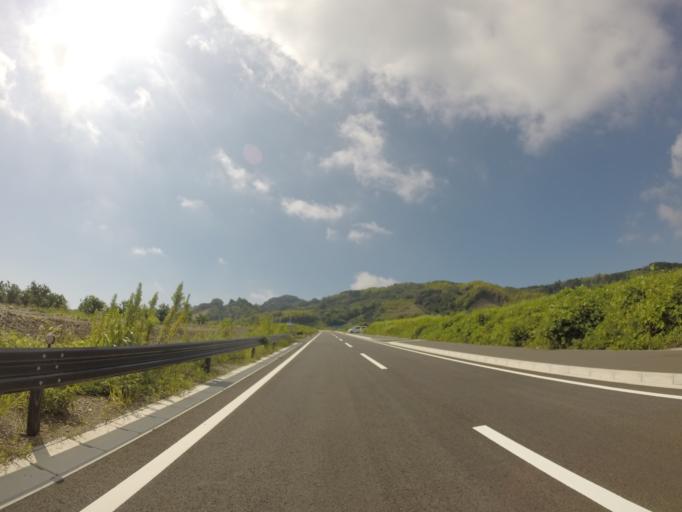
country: JP
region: Shizuoka
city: Shizuoka-shi
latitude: 34.9896
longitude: 138.4689
